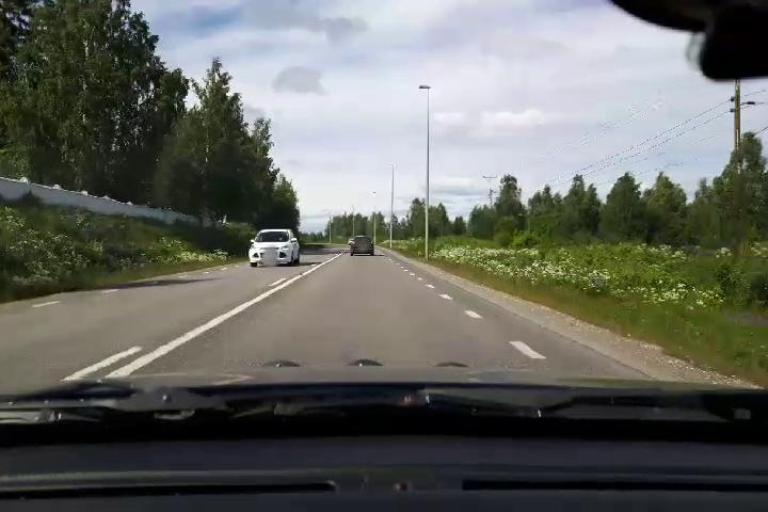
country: SE
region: Gaevleborg
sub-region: Bollnas Kommun
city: Bollnas
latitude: 61.3631
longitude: 16.3962
